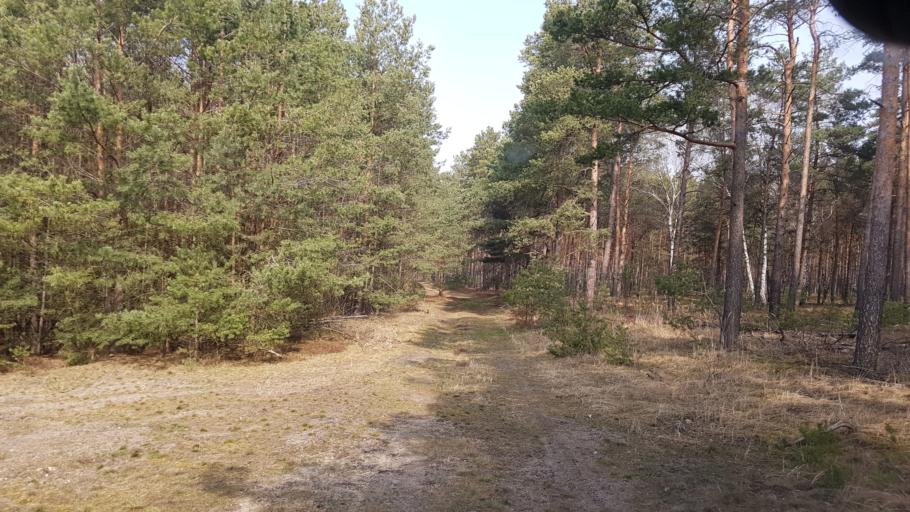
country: DE
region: Brandenburg
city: Schilda
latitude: 51.6232
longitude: 13.4071
